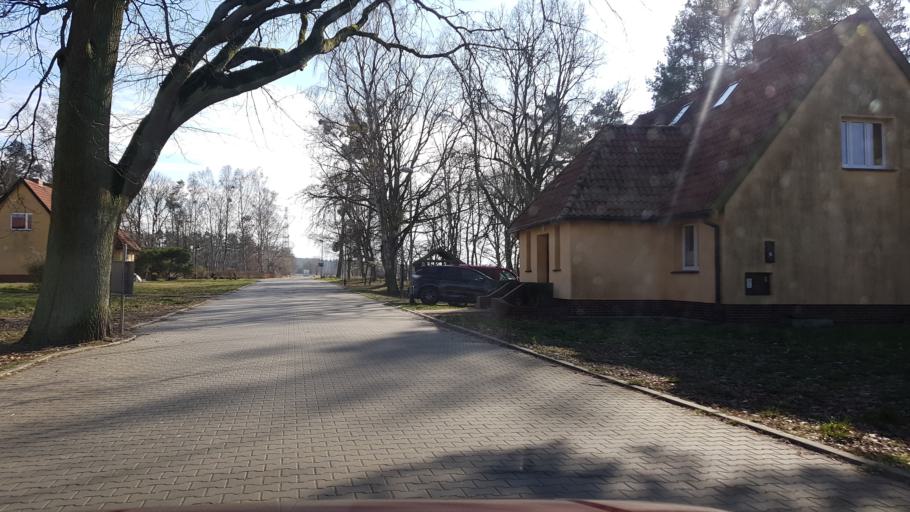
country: PL
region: West Pomeranian Voivodeship
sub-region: Powiat policki
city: Nowe Warpno
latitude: 53.7349
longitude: 14.3086
